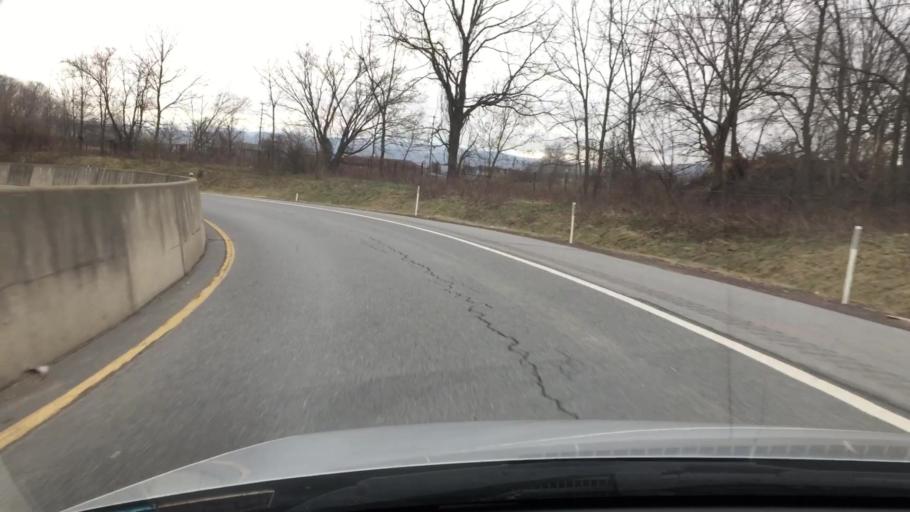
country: US
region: Pennsylvania
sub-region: Columbia County
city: Light Street
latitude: 41.0254
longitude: -76.4256
